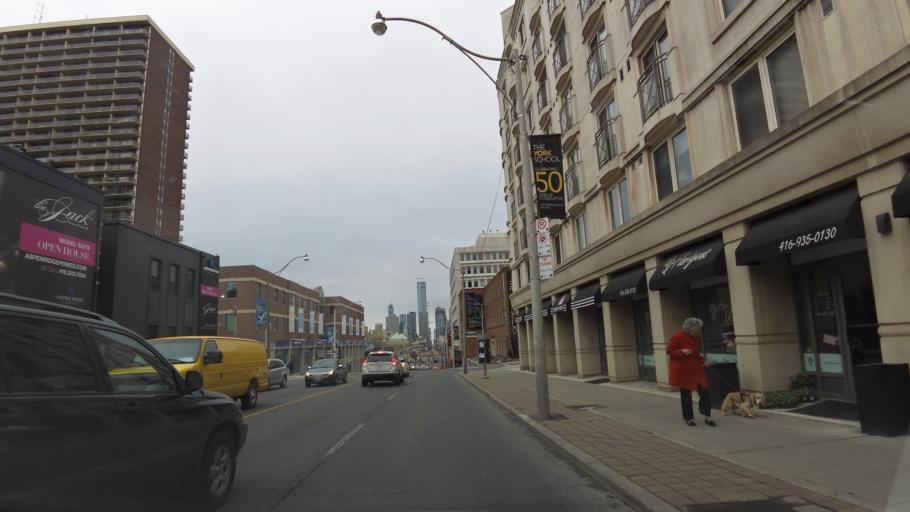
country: CA
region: Ontario
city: Toronto
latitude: 43.6854
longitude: -79.3928
